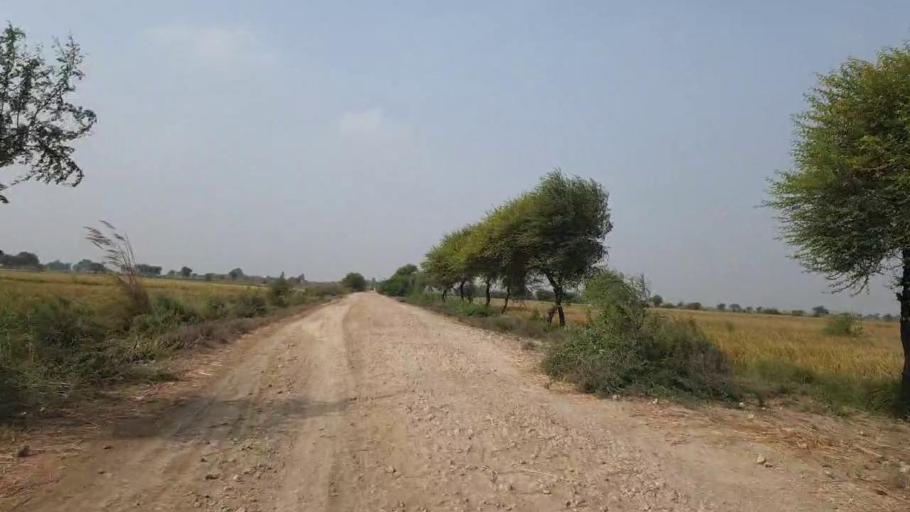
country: PK
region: Sindh
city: Kario
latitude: 24.7602
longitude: 68.5446
